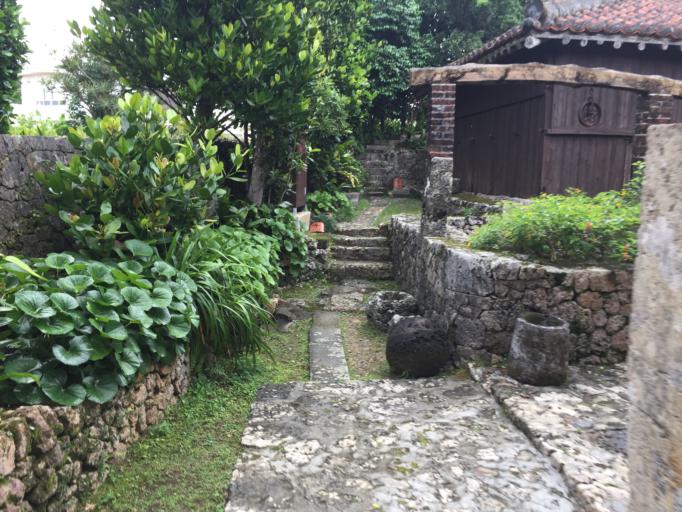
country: JP
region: Okinawa
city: Chatan
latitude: 26.2897
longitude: 127.8007
